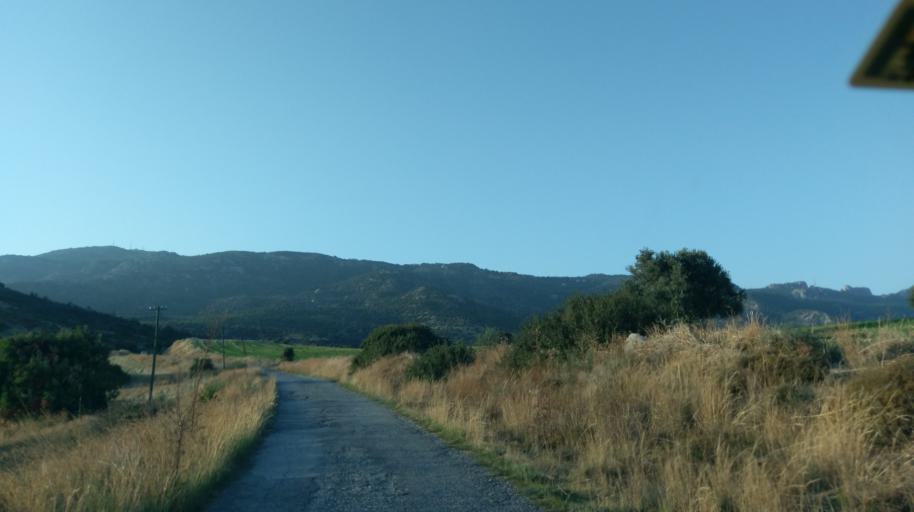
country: CY
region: Ammochostos
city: Trikomo
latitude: 35.3671
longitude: 33.9106
